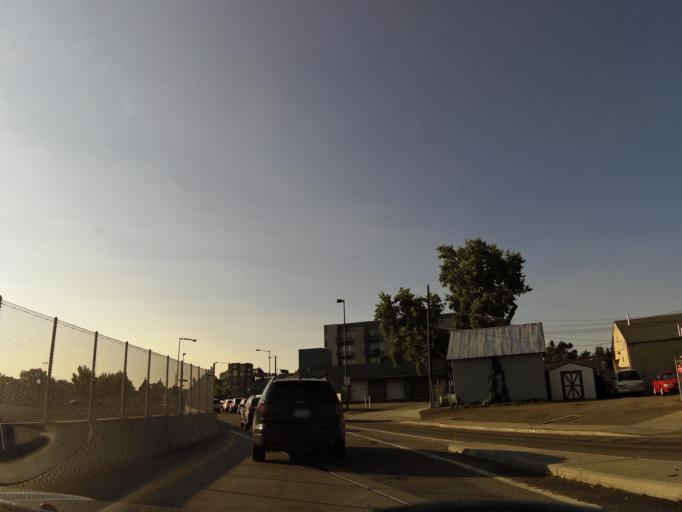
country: US
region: Colorado
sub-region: Denver County
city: Denver
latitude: 39.6943
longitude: -104.9800
